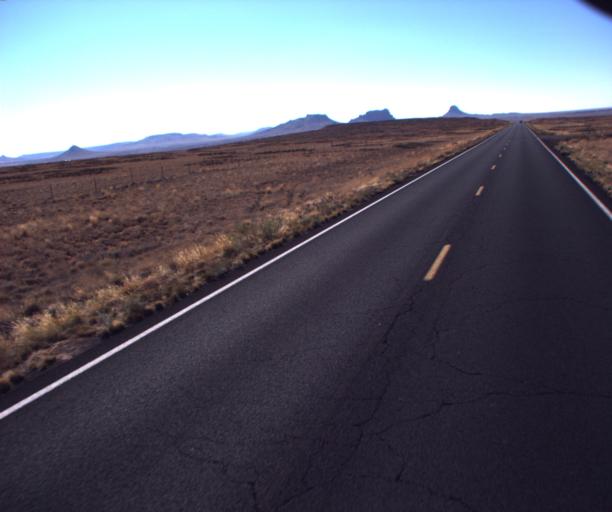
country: US
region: Arizona
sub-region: Navajo County
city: Dilkon
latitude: 35.4024
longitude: -110.4262
